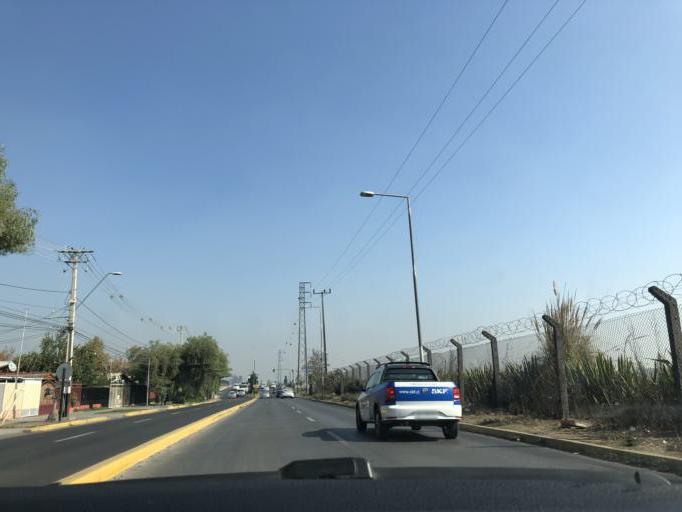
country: CL
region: Santiago Metropolitan
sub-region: Provincia de Cordillera
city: Puente Alto
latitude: -33.6060
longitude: -70.6014
